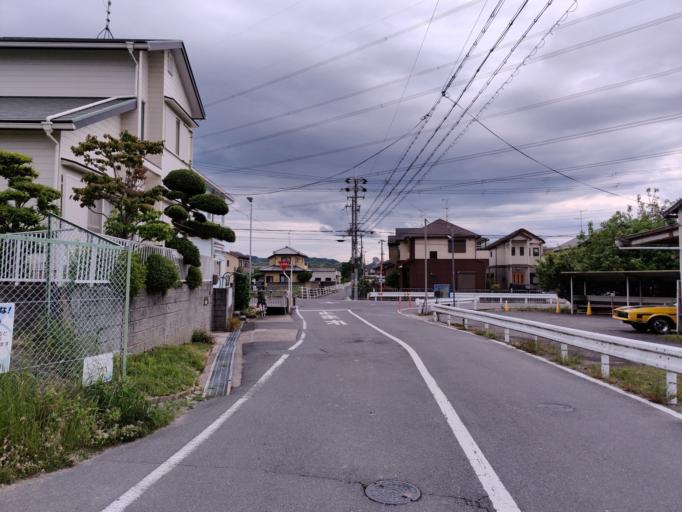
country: JP
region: Kyoto
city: Tanabe
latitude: 34.7577
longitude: 135.7968
